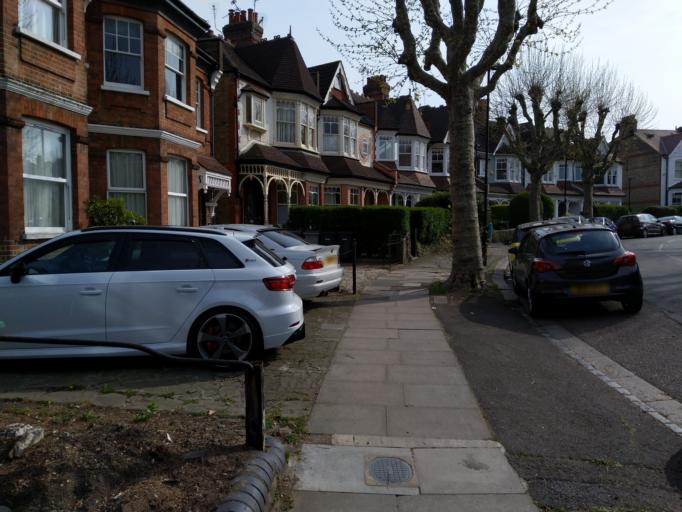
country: GB
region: England
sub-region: Greater London
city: Crouch End
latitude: 51.5862
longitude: -0.1275
